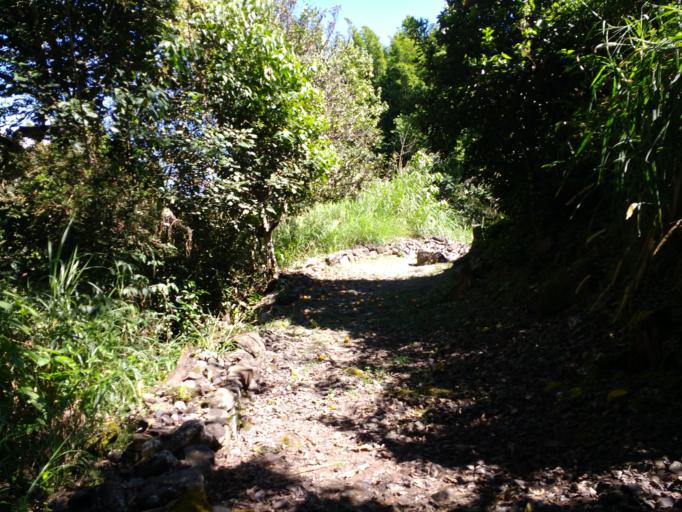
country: PE
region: Cusco
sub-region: Provincia de La Convencion
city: Maranura
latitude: -13.0047
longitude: -72.5340
